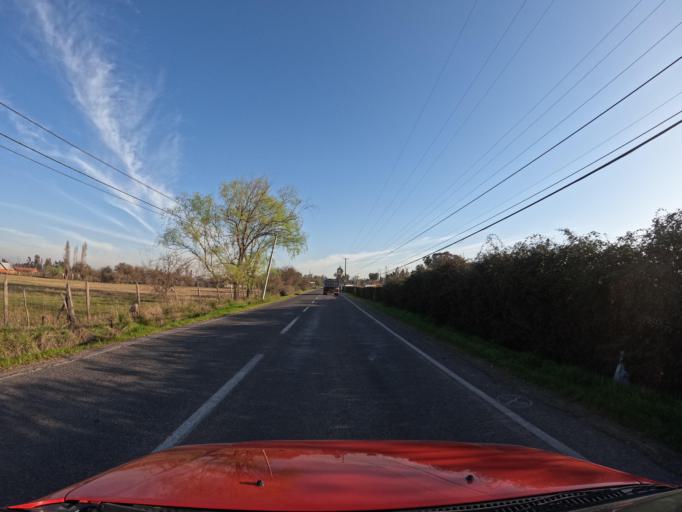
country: CL
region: Maule
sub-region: Provincia de Curico
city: Rauco
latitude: -34.8759
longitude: -71.2678
